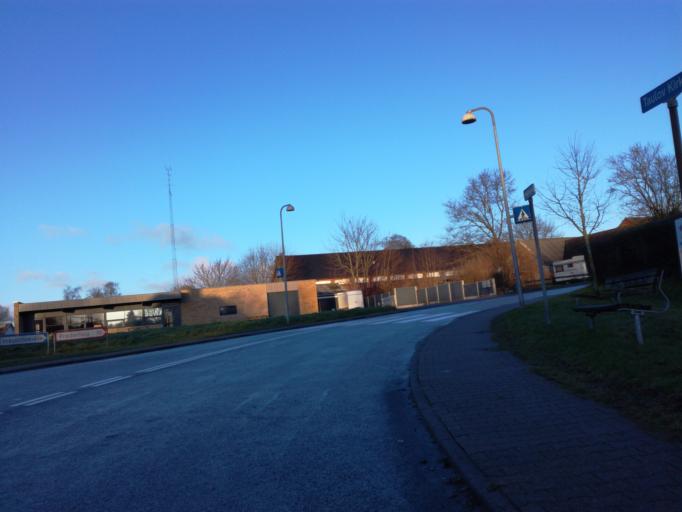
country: DK
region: South Denmark
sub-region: Fredericia Kommune
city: Taulov
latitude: 55.5453
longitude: 9.6132
